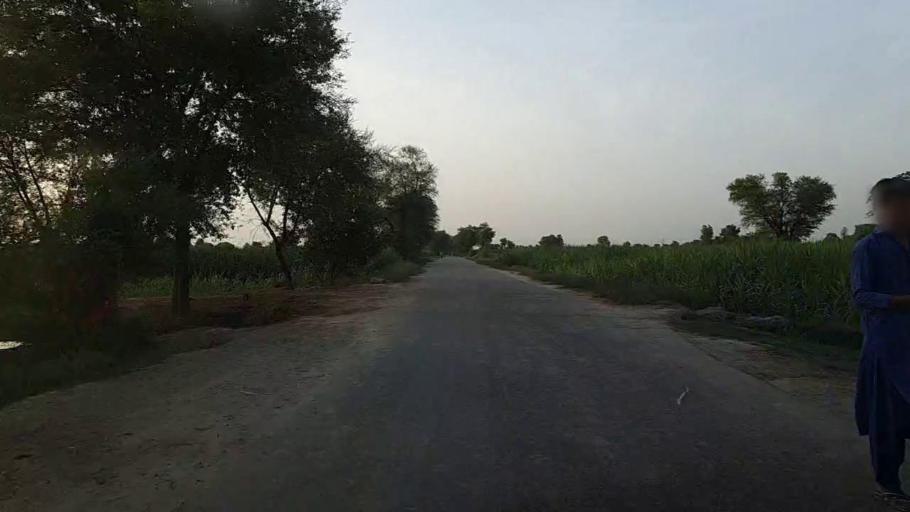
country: PK
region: Sindh
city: Ubauro
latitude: 28.2313
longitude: 69.8159
